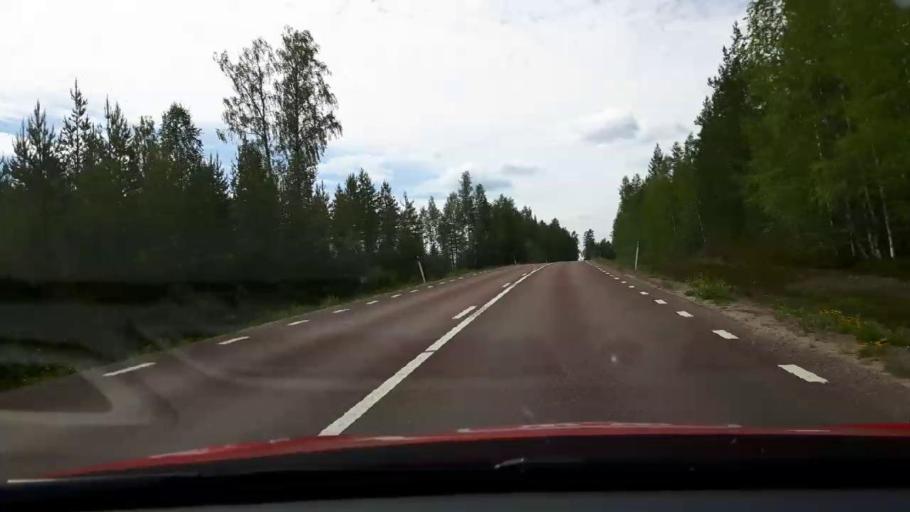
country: SE
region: Jaemtland
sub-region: Harjedalens Kommun
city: Sveg
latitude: 62.0494
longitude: 14.8915
